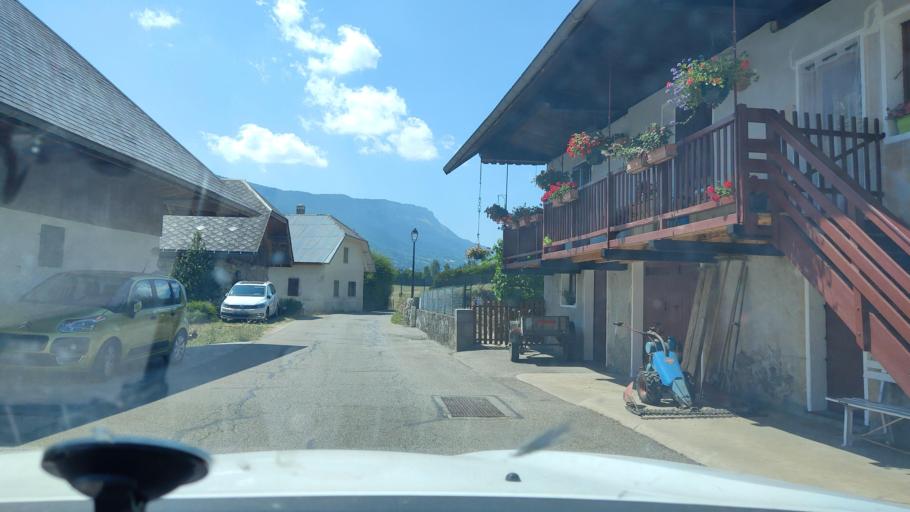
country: FR
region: Rhone-Alpes
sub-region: Departement de la Haute-Savoie
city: Cusy
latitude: 45.7134
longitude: 6.0863
